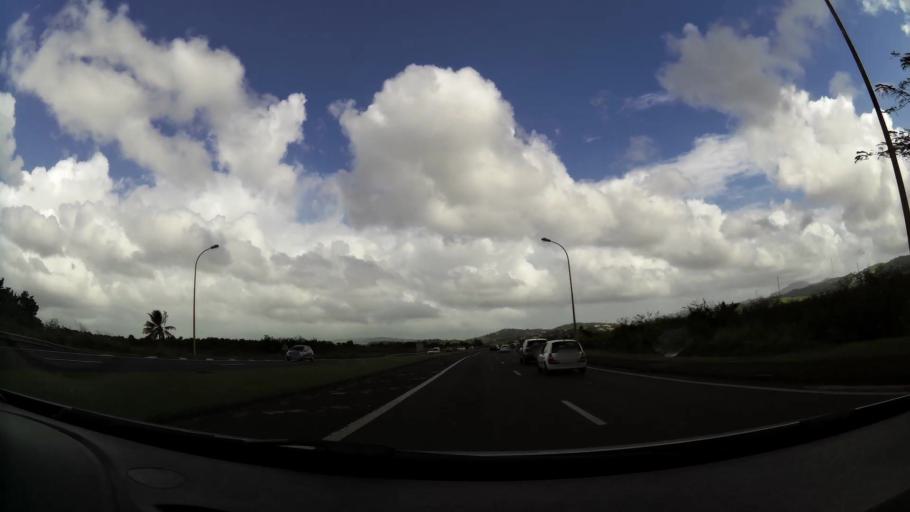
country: MQ
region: Martinique
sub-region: Martinique
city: Ducos
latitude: 14.5332
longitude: -60.9828
